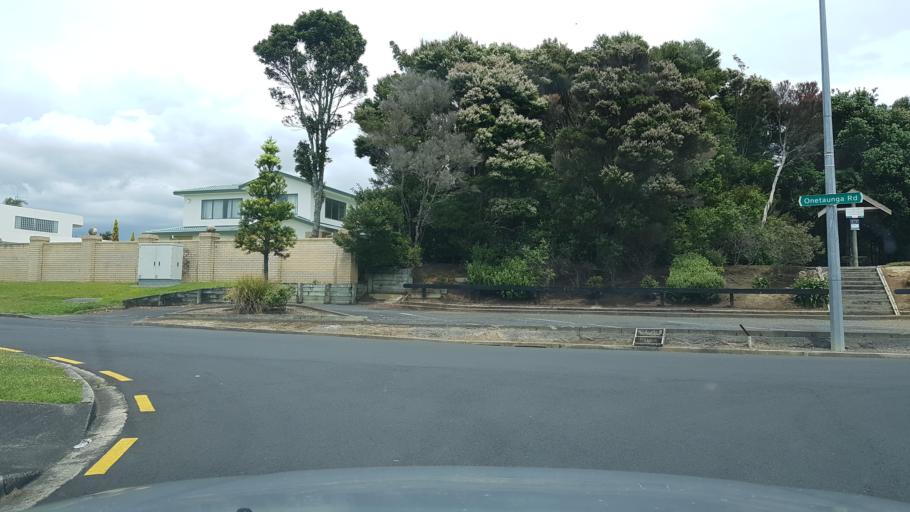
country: NZ
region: Auckland
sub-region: Auckland
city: North Shore
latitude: -36.8218
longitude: 174.7114
